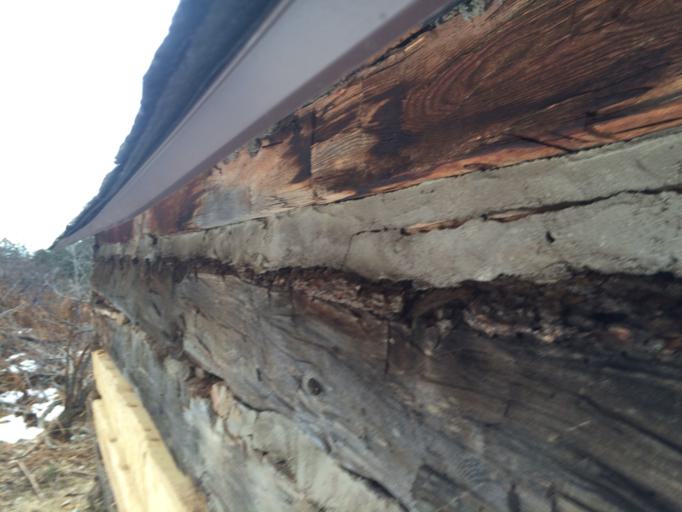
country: US
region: Colorado
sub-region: Boulder County
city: Boulder
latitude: 39.9436
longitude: -105.2818
